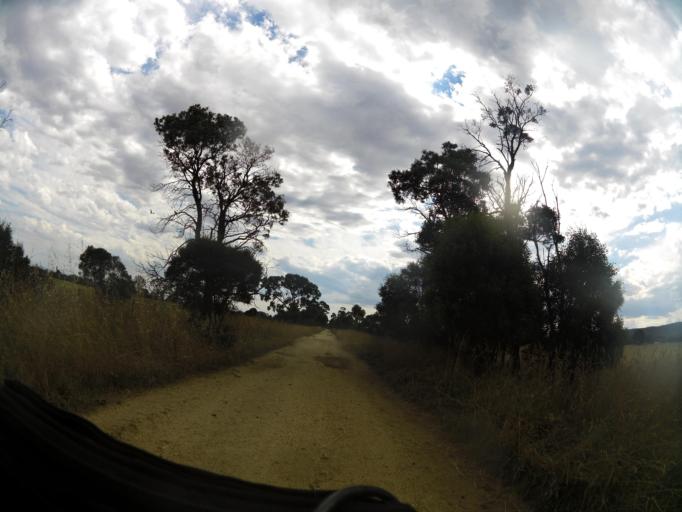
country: AU
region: Victoria
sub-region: Wellington
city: Heyfield
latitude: -38.0459
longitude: 146.6380
